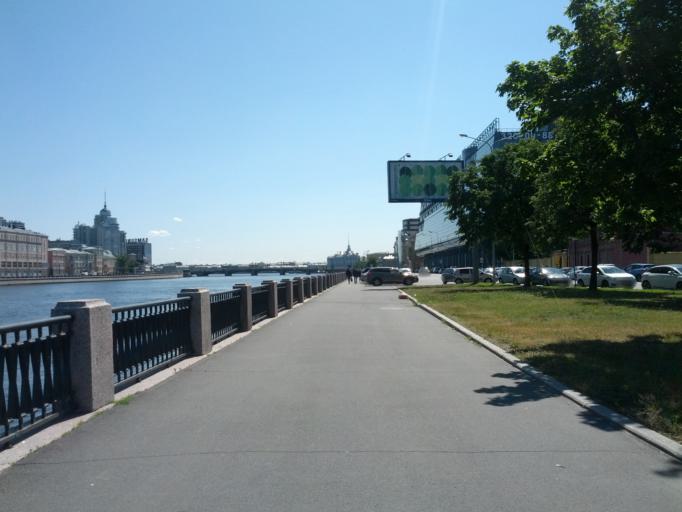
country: RU
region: Leningrad
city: Sampsonievskiy
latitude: 59.9649
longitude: 30.3347
